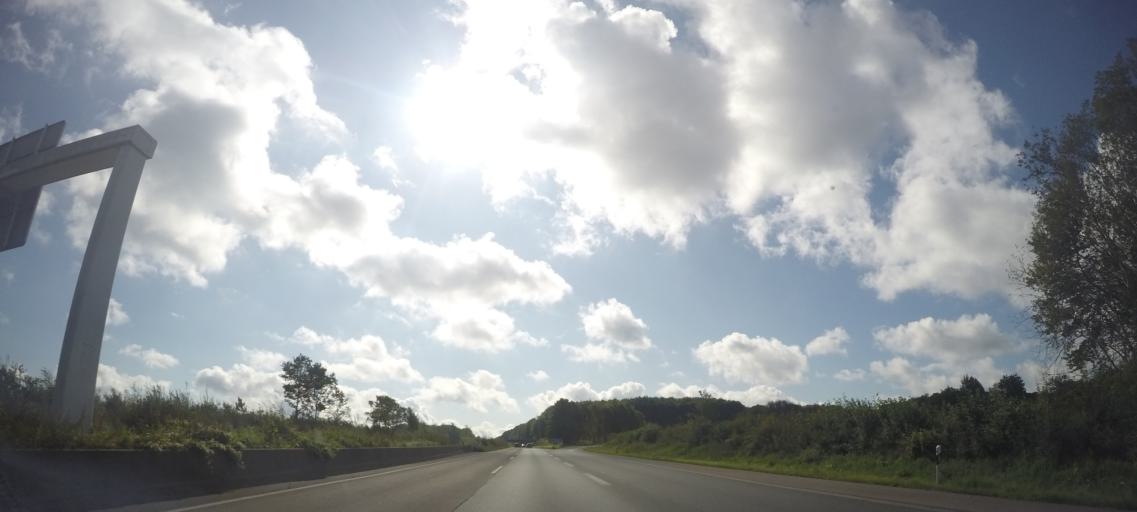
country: DE
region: North Rhine-Westphalia
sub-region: Regierungsbezirk Arnsberg
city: Werl
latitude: 51.5227
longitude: 7.8972
